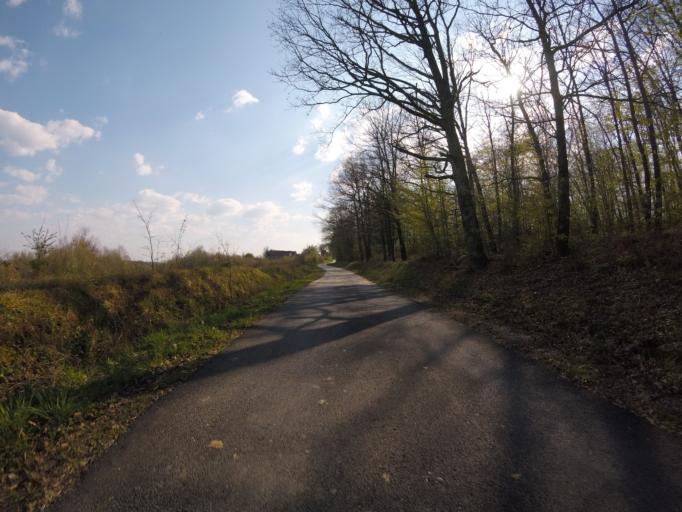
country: HR
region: Sisacko-Moslavacka
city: Glina
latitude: 45.4989
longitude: 16.0061
